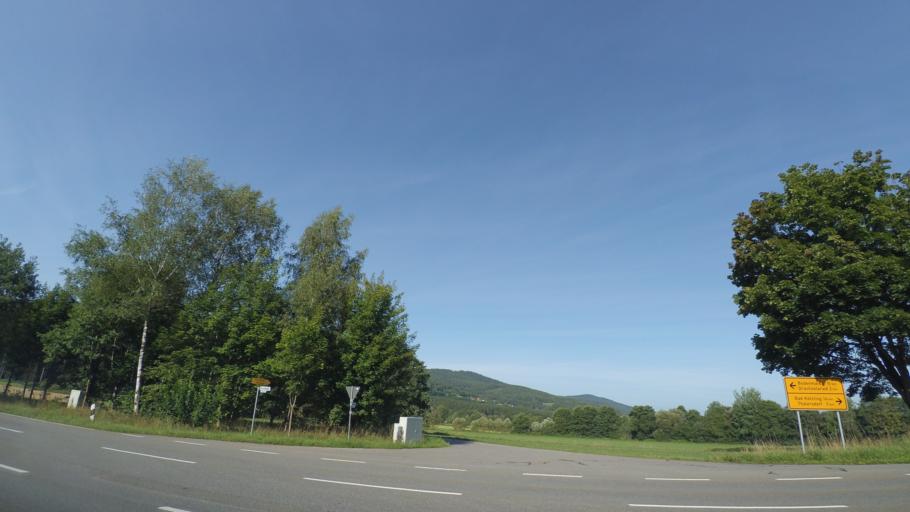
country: DE
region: Bavaria
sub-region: Lower Bavaria
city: Arnbruck
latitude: 49.1209
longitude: 12.9986
